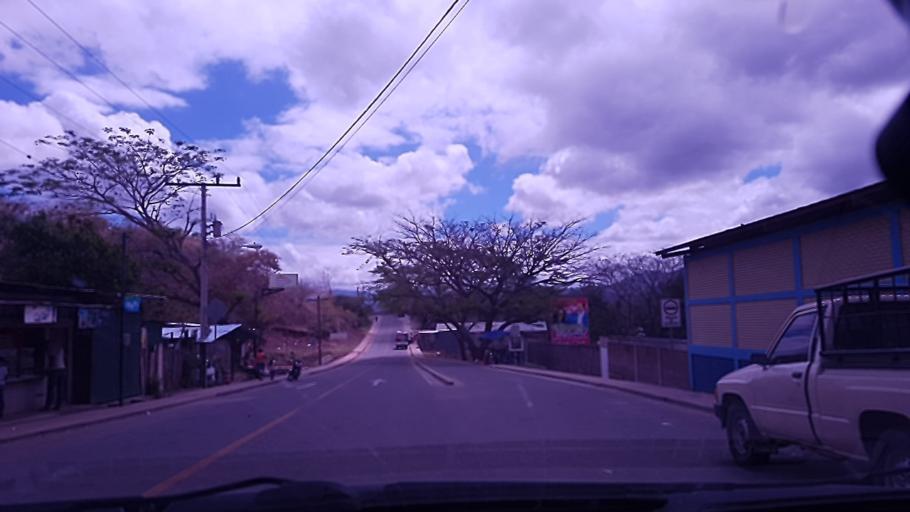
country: NI
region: Esteli
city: Condega
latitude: 13.3712
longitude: -86.3994
